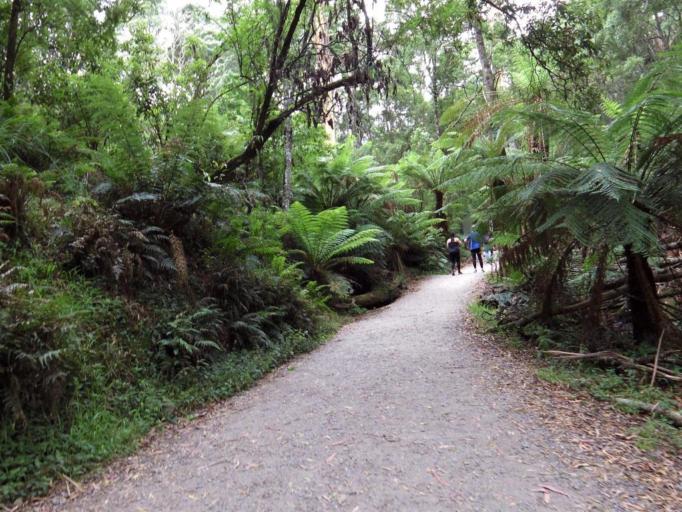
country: AU
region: Victoria
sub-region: Yarra Ranges
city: Ferny Creek
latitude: -37.8811
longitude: 145.3183
